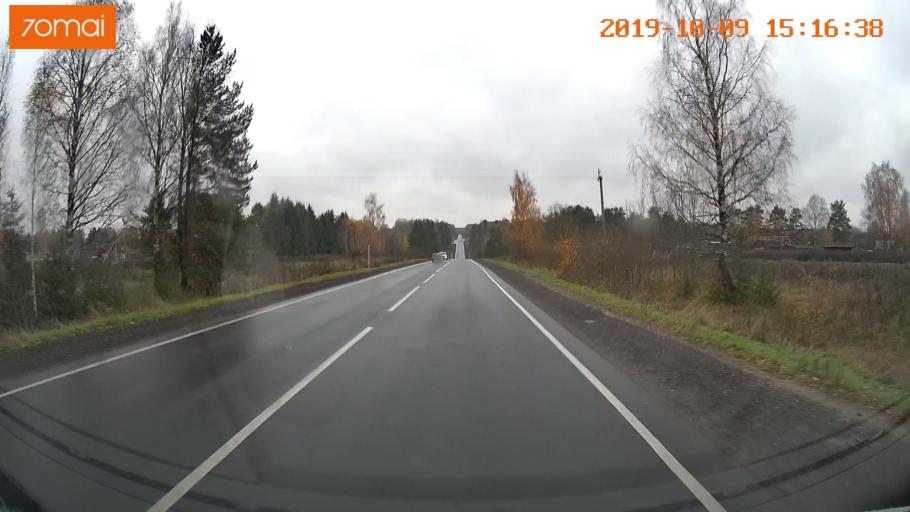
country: RU
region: Kostroma
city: Susanino
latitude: 58.1084
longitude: 41.5854
